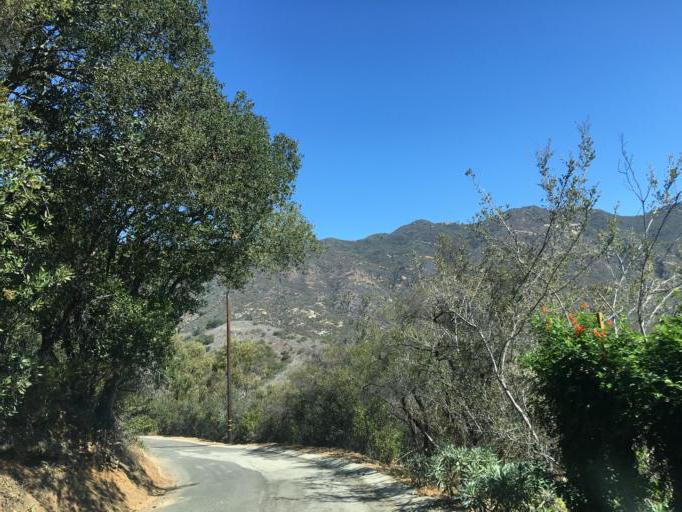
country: US
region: California
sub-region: Los Angeles County
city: Malibu Beach
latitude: 34.0623
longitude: -118.7388
